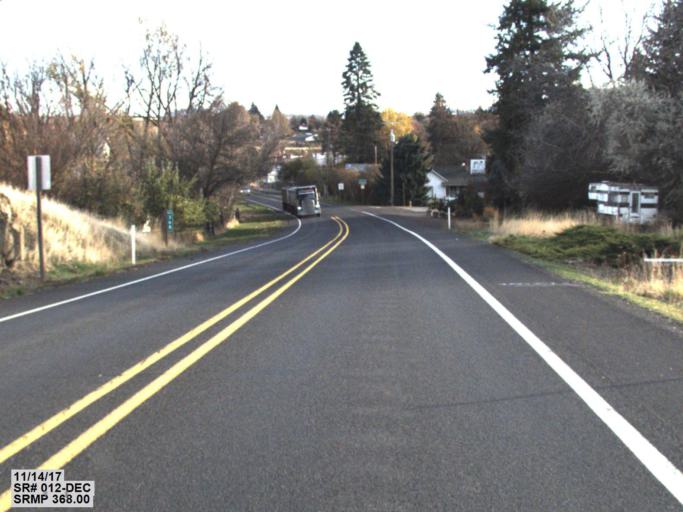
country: US
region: Washington
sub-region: Columbia County
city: Dayton
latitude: 46.3285
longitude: -117.9753
